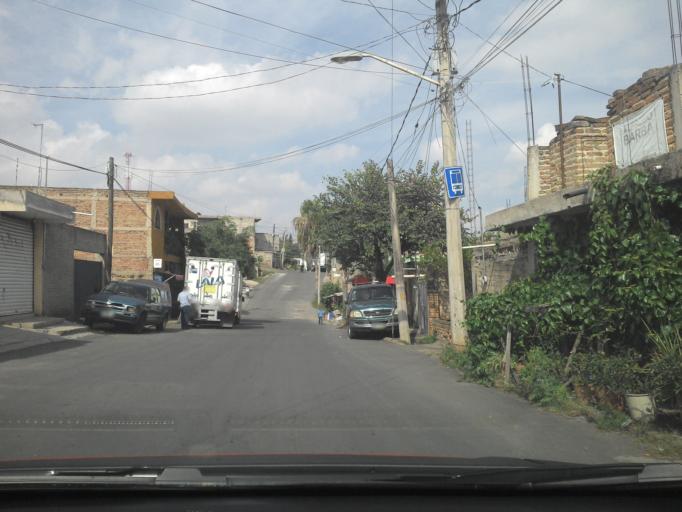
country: MX
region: Jalisco
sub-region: Tlajomulco de Zuniga
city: Altus Bosques
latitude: 20.5957
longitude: -103.3511
